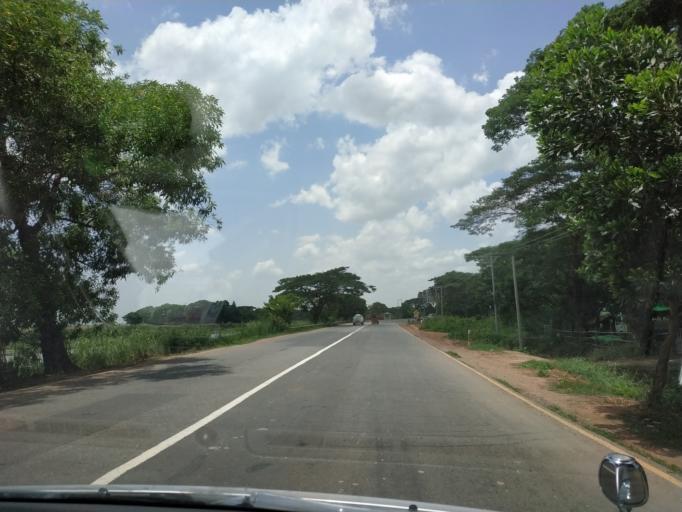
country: MM
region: Bago
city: Thanatpin
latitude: 17.5148
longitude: 96.7163
